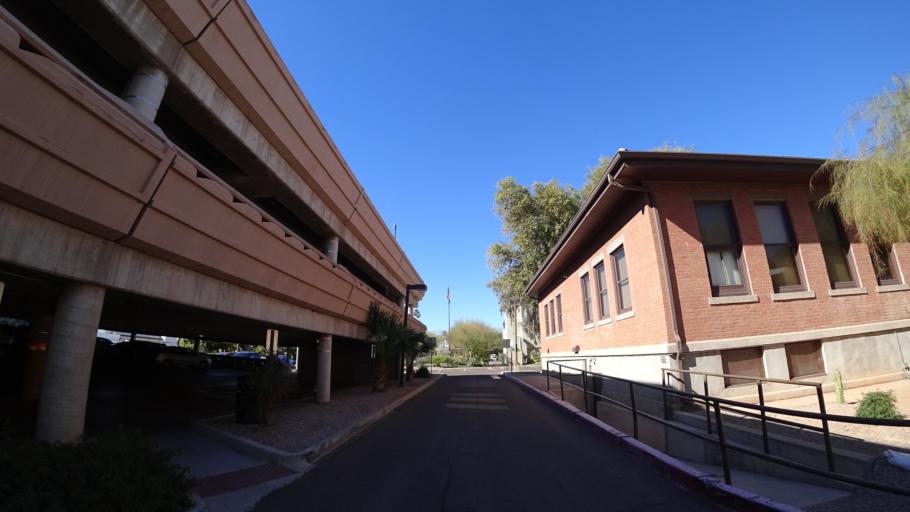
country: US
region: Arizona
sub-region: Maricopa County
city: Scottsdale
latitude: 33.4927
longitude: -111.9234
